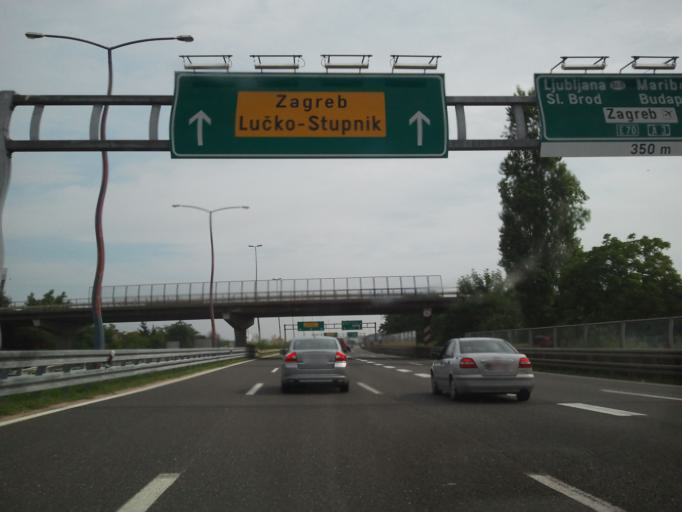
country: HR
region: Grad Zagreb
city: Brezovica
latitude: 45.7517
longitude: 15.8869
